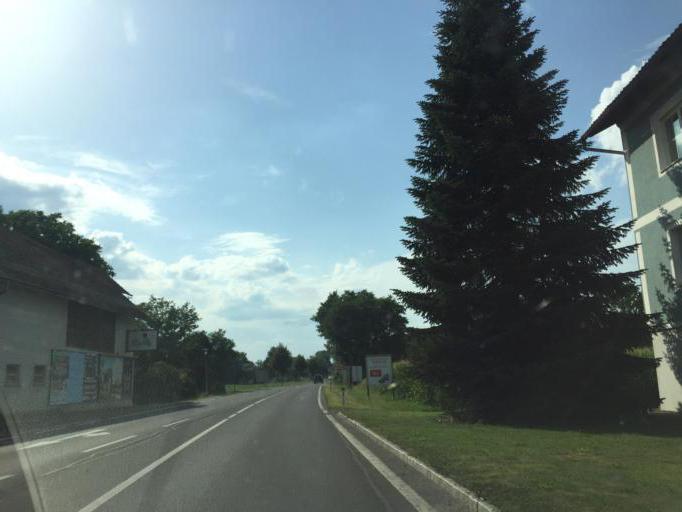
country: AT
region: Styria
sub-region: Politischer Bezirk Suedoststeiermark
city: Bad Radkersburg
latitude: 46.6921
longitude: 15.9762
